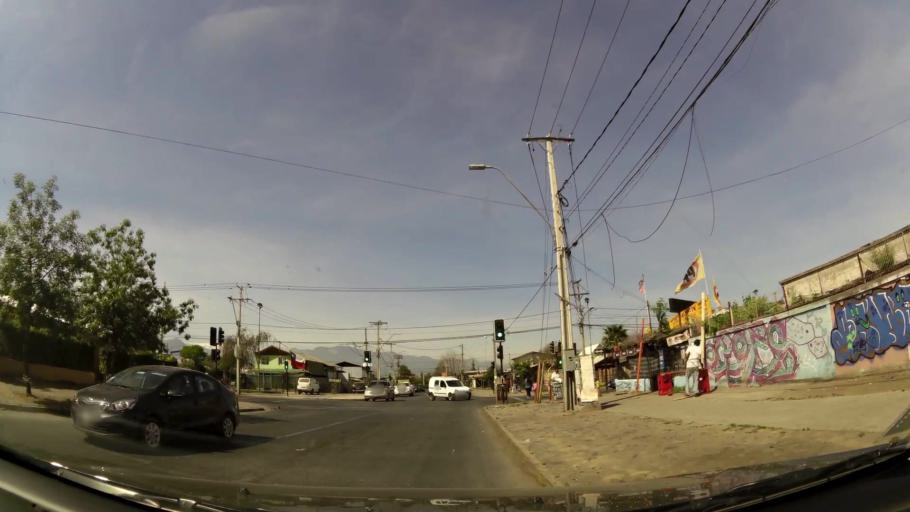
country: CL
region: Santiago Metropolitan
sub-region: Provincia de Cordillera
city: Puente Alto
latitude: -33.6152
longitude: -70.5868
